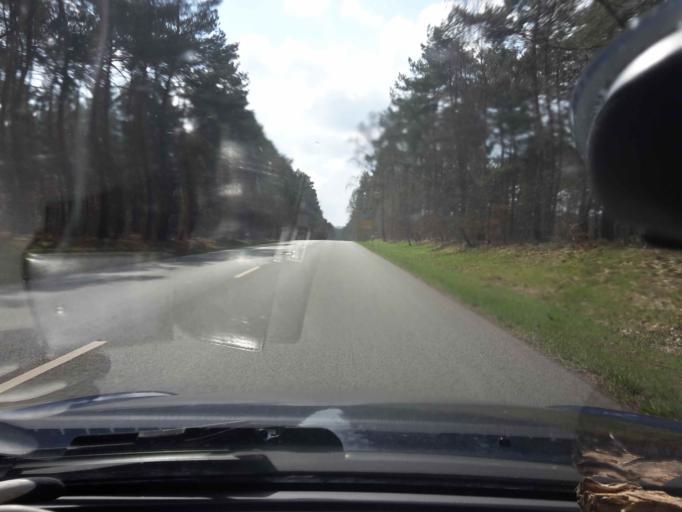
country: DE
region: Lower Saxony
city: Munster
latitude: 53.0225
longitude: 10.0541
